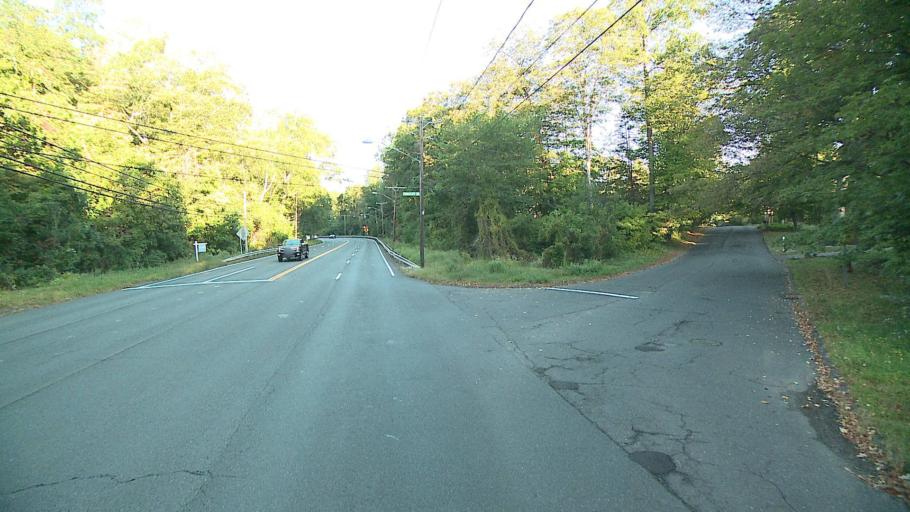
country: US
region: Connecticut
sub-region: Hartford County
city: West Hartford
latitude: 41.7896
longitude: -72.7748
